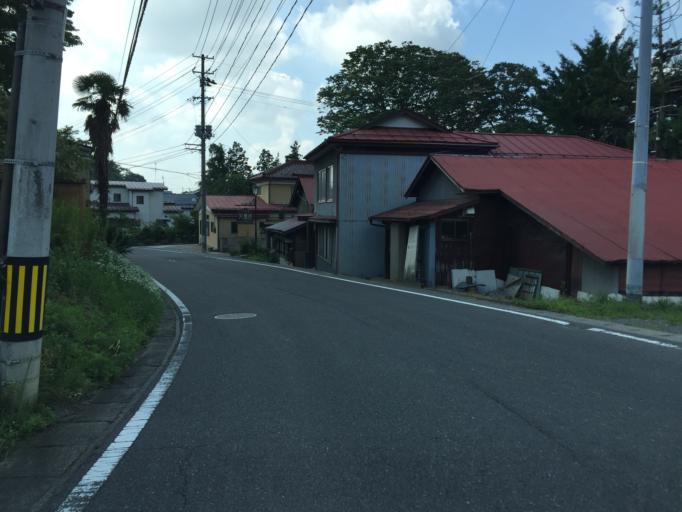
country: JP
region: Fukushima
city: Motomiya
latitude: 37.5246
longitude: 140.4033
